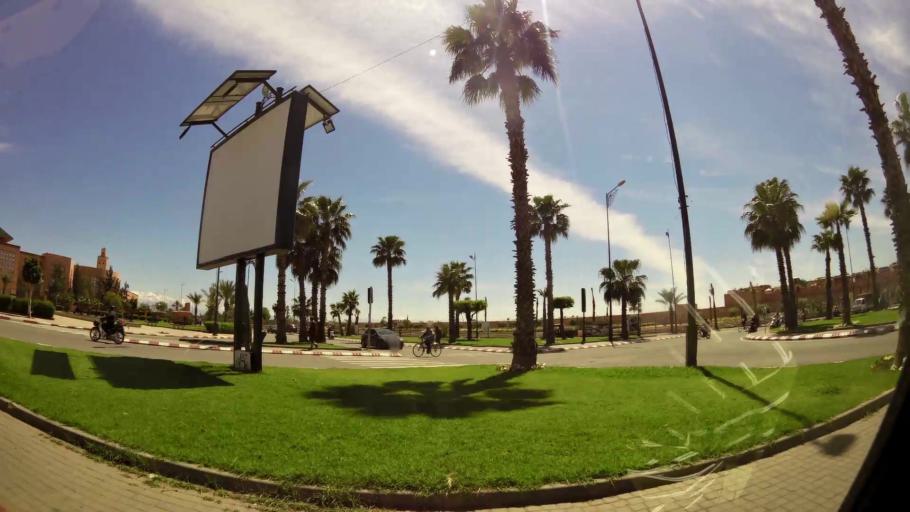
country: MA
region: Marrakech-Tensift-Al Haouz
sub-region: Marrakech
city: Marrakesh
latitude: 31.6145
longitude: -7.9747
